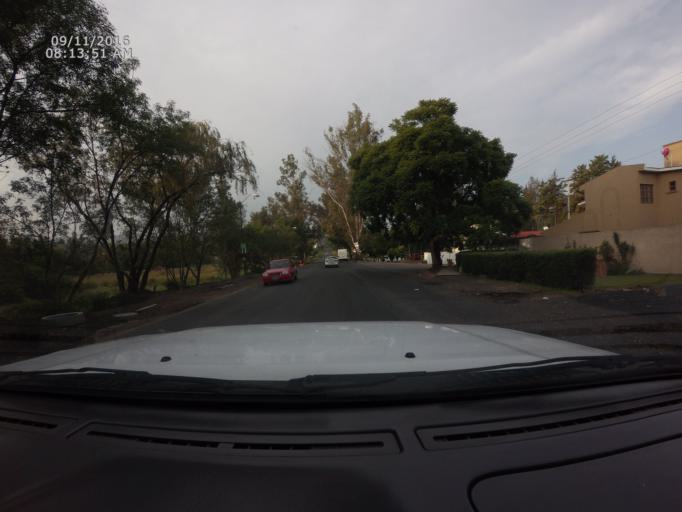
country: MX
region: Michoacan
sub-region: Morelia
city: Morelos
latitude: 19.6629
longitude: -101.2261
